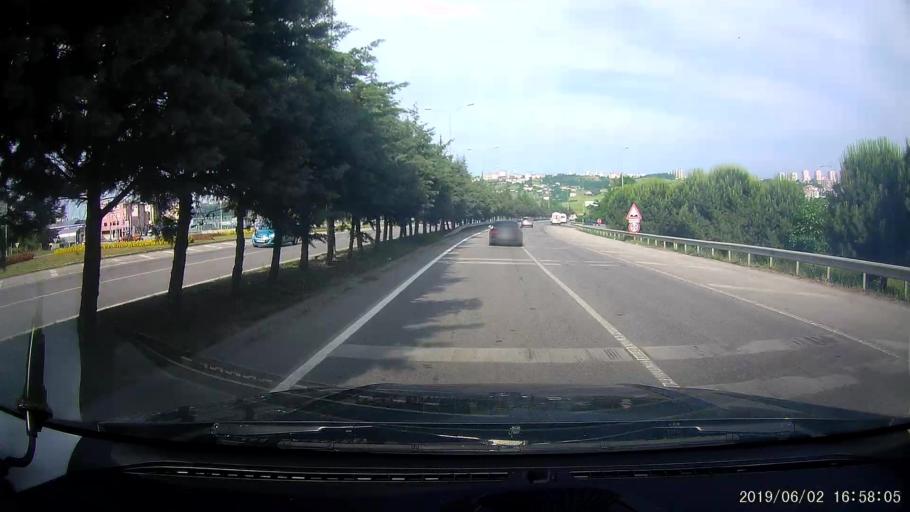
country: TR
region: Samsun
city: Samsun
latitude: 41.2904
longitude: 36.2846
